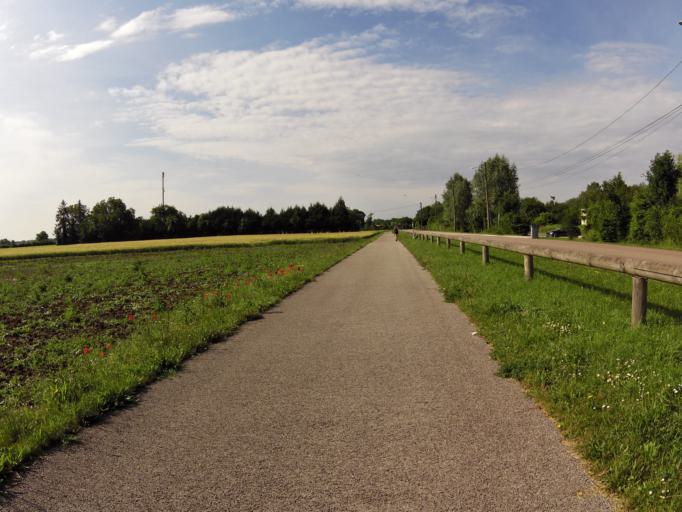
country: FR
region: Champagne-Ardenne
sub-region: Departement de l'Aube
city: Saint-Julien-les-Villas
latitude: 48.2748
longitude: 4.1117
